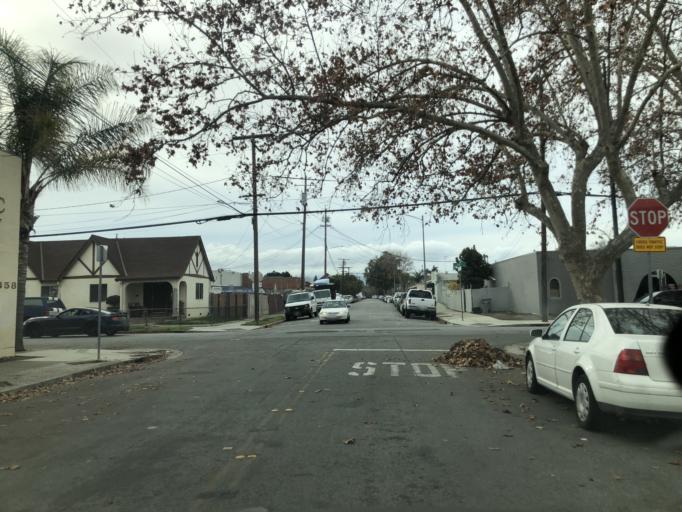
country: US
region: California
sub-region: Santa Clara County
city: San Jose
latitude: 37.3473
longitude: -121.8626
